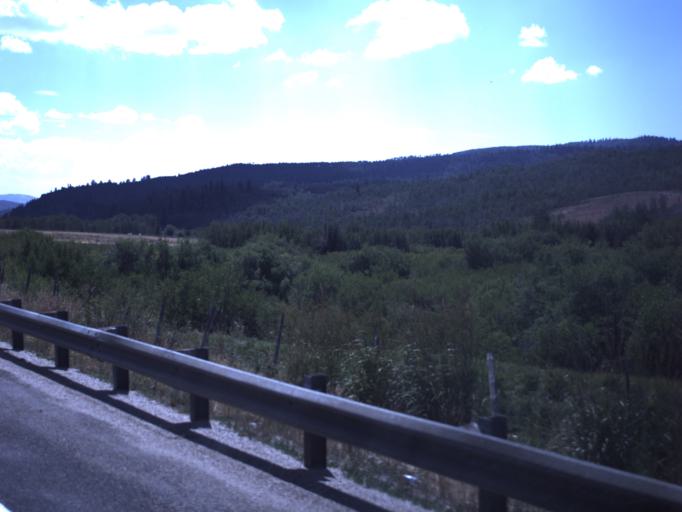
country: US
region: Utah
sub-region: Cache County
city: Richmond
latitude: 41.9251
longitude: -111.5605
